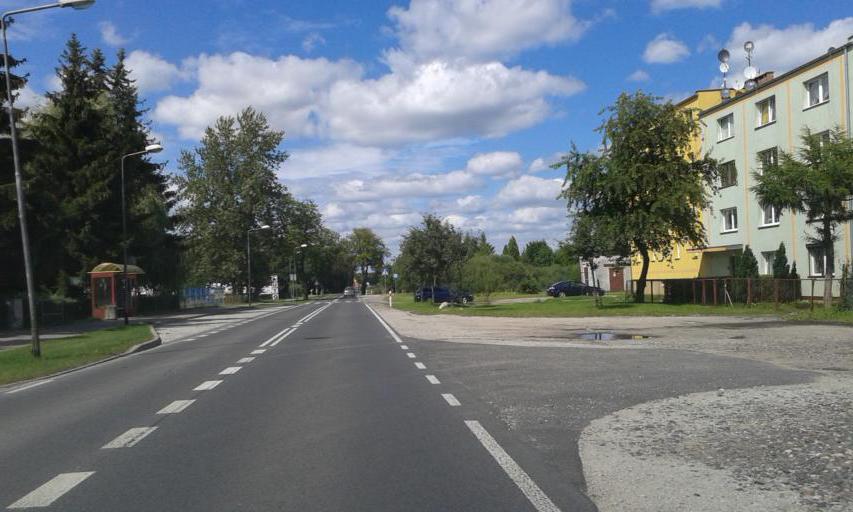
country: PL
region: West Pomeranian Voivodeship
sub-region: Powiat walecki
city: Walcz
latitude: 53.2869
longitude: 16.4603
